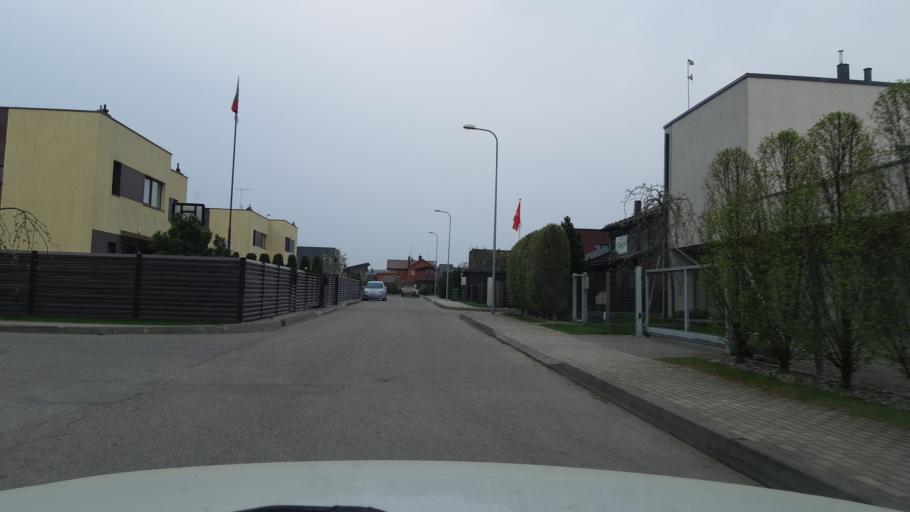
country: LT
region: Kauno apskritis
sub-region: Kaunas
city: Sargenai
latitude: 54.9454
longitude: 23.9032
